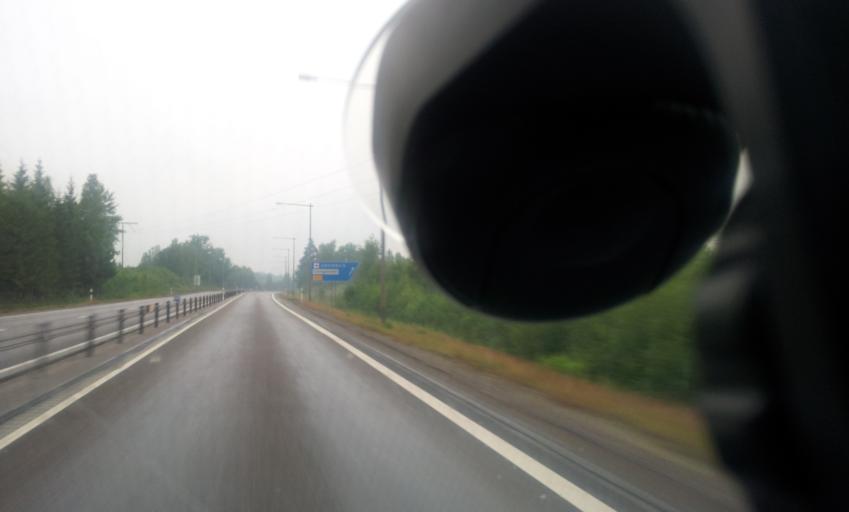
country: SE
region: Kalmar
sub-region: Vasterviks Kommun
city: Vaestervik
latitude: 57.7570
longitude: 16.5568
